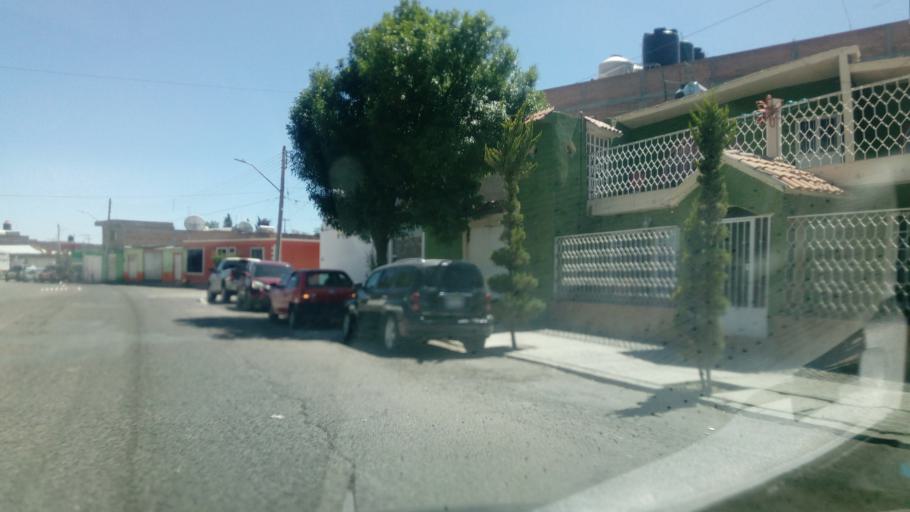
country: MX
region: Durango
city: Victoria de Durango
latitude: 24.0149
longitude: -104.6573
